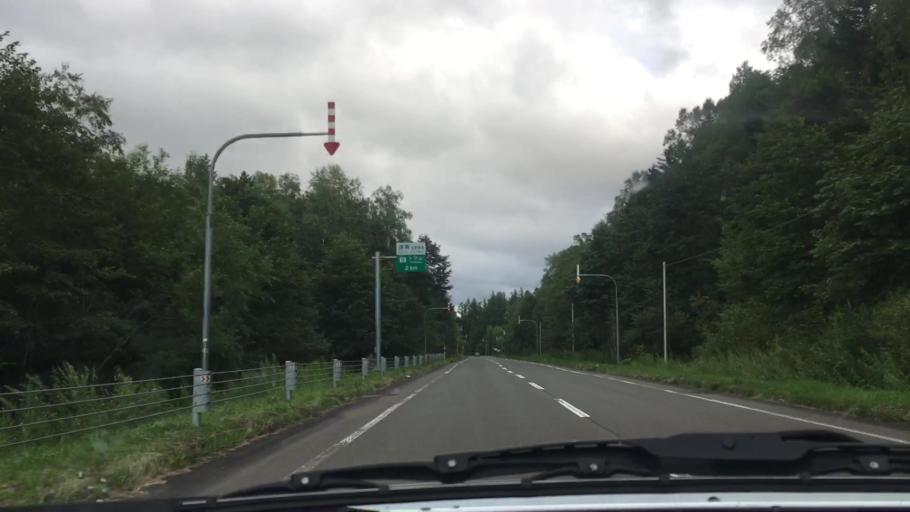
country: JP
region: Hokkaido
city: Shimo-furano
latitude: 43.0576
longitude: 142.6683
